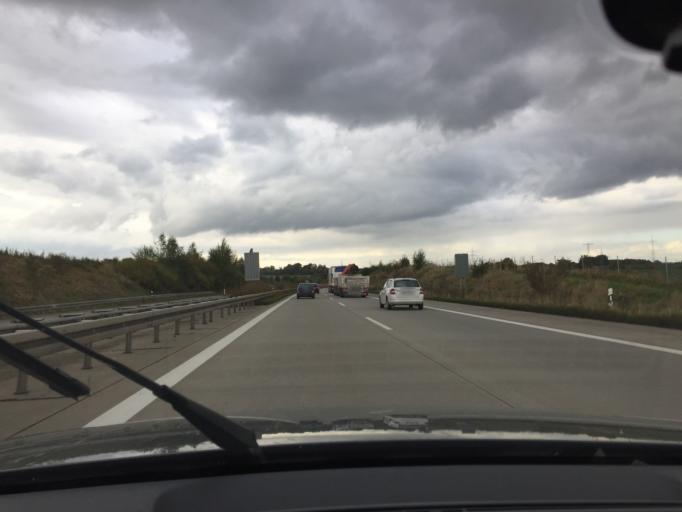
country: DE
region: Saxony
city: Bannewitz
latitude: 50.9985
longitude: 13.7543
